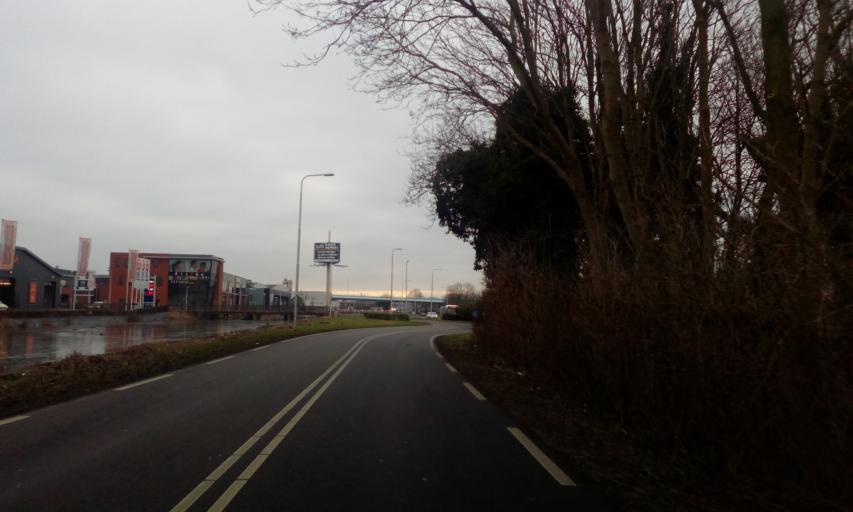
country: NL
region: South Holland
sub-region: Gemeente Waddinxveen
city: Waddinxveen
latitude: 52.0278
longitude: 4.6604
